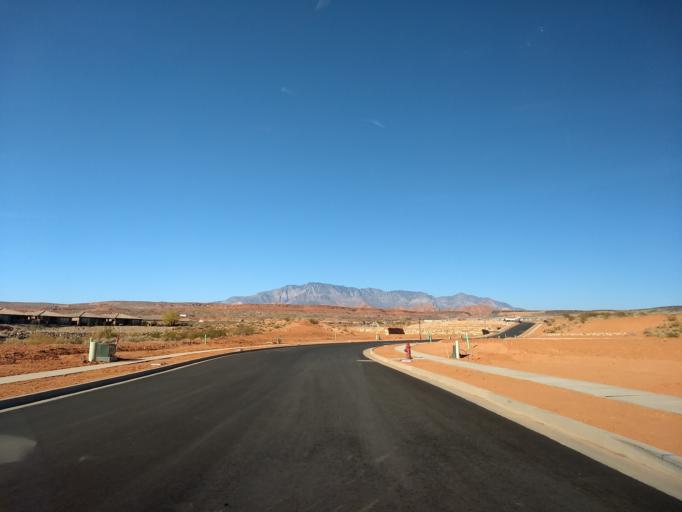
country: US
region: Utah
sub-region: Washington County
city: Washington
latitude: 37.1386
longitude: -113.4806
